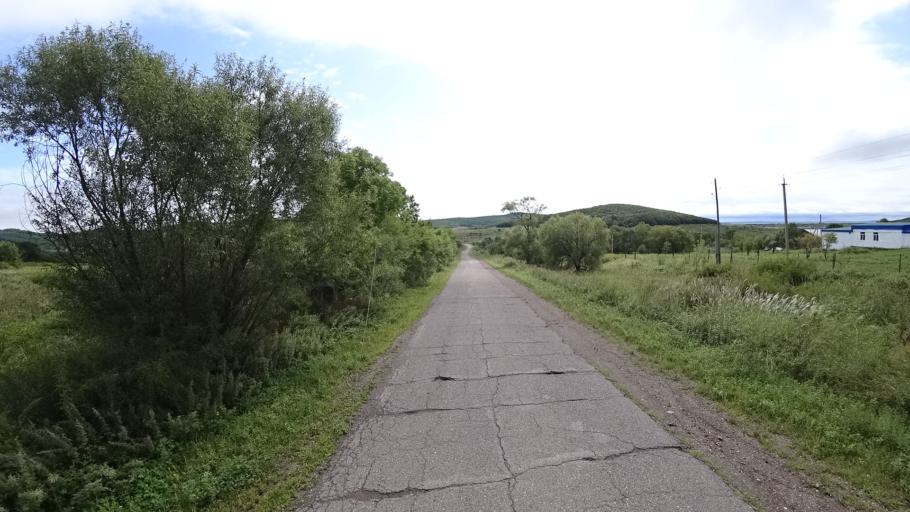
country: RU
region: Primorskiy
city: Lyalichi
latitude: 44.1406
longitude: 132.3883
